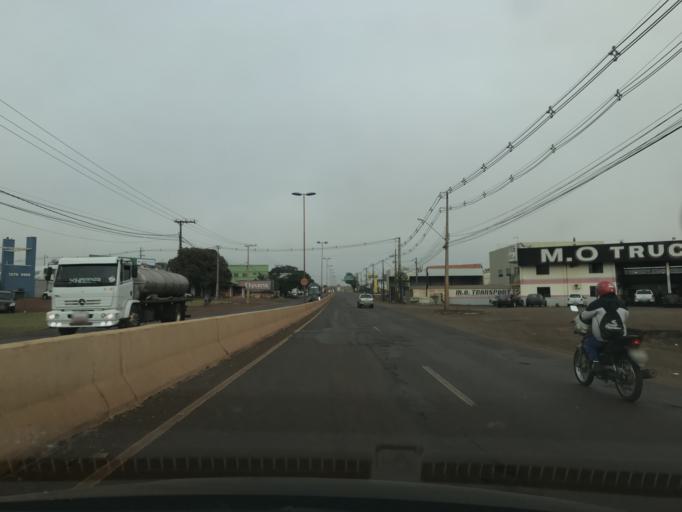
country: BR
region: Parana
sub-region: Toledo
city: Toledo
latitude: -24.7153
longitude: -53.7058
